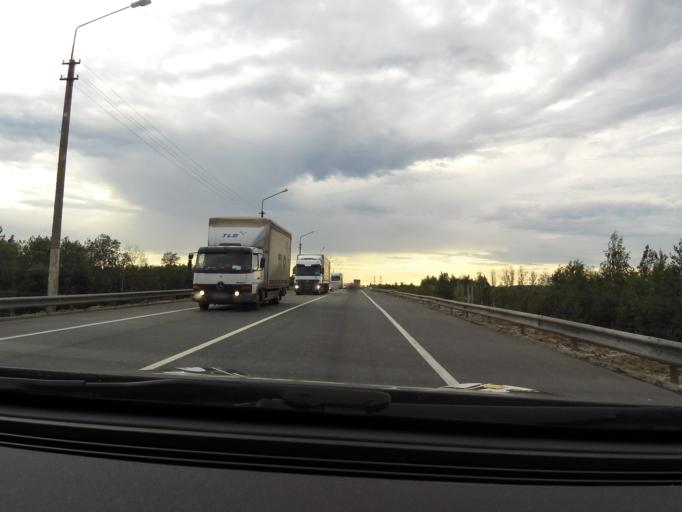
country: RU
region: Vladimir
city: Vorsha
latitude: 56.0748
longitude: 40.2156
